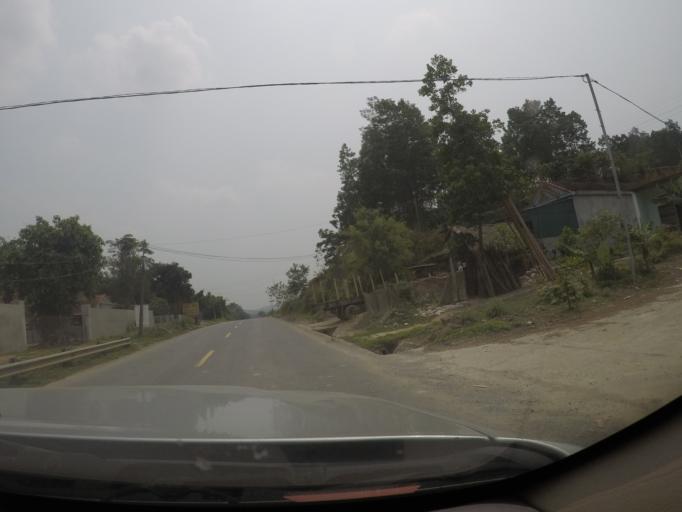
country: VN
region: Thanh Hoa
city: Thi Tran Yen Cat
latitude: 19.7831
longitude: 105.4033
